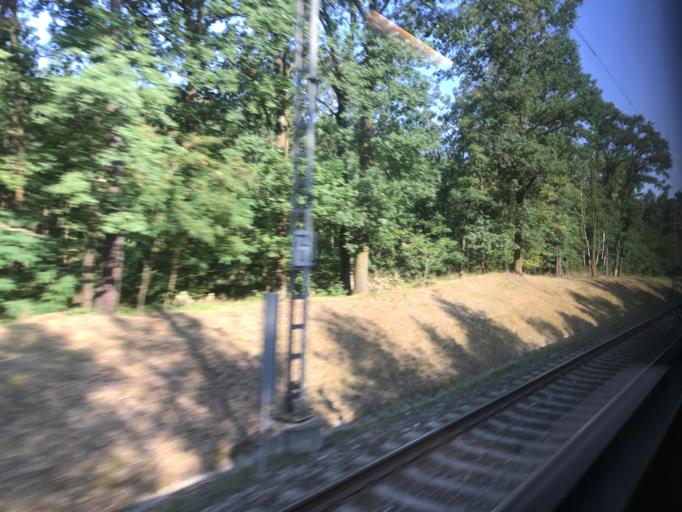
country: CZ
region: Jihocesky
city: Plana nad Luznici
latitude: 49.3318
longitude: 14.7142
